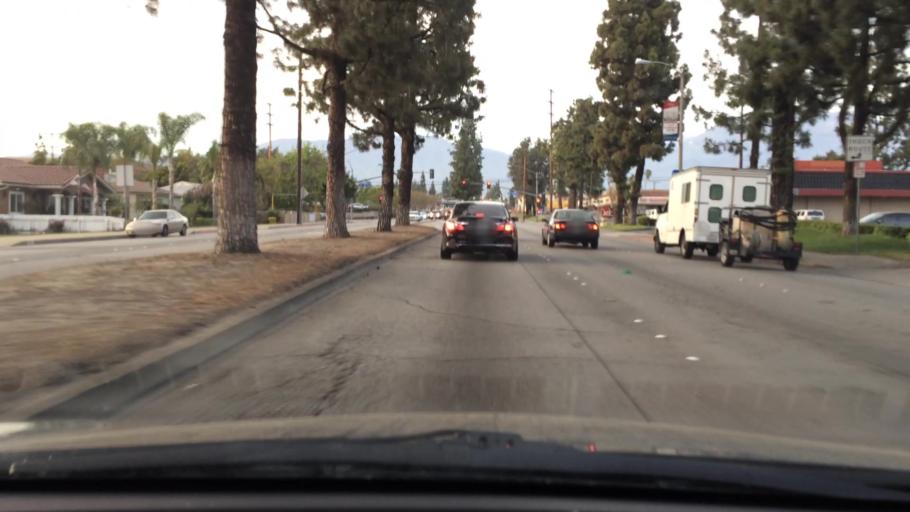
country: US
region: California
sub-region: San Bernardino County
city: Montclair
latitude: 34.0802
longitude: -117.6896
